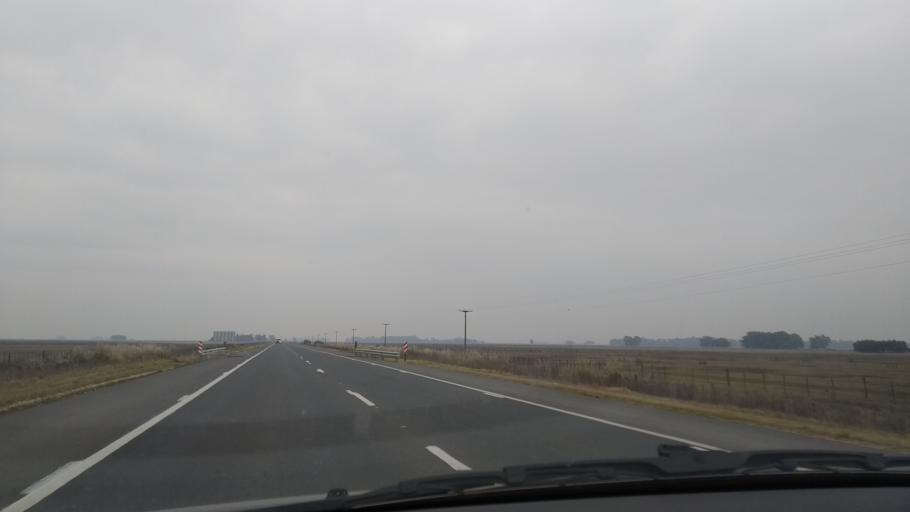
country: AR
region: Buenos Aires
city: Olavarria
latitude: -36.9920
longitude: -60.3197
